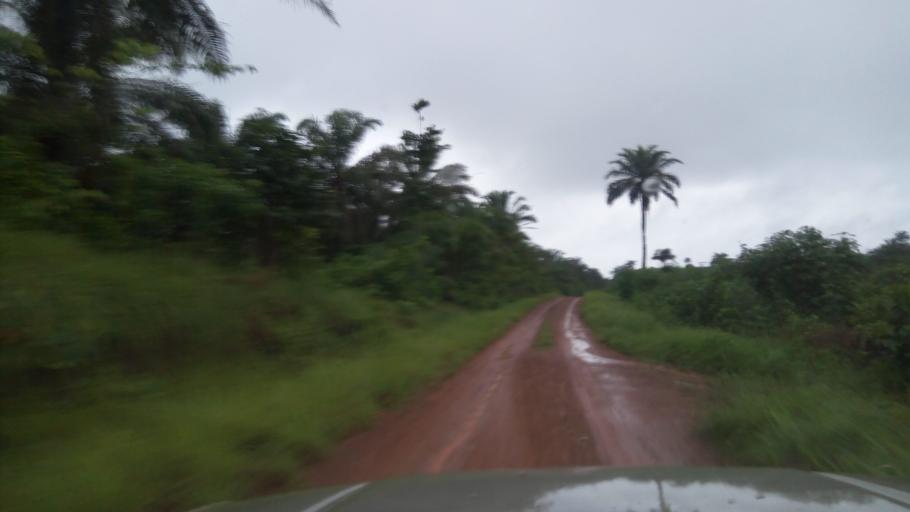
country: SL
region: Southern Province
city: Zimmi
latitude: 7.2749
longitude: -11.2398
